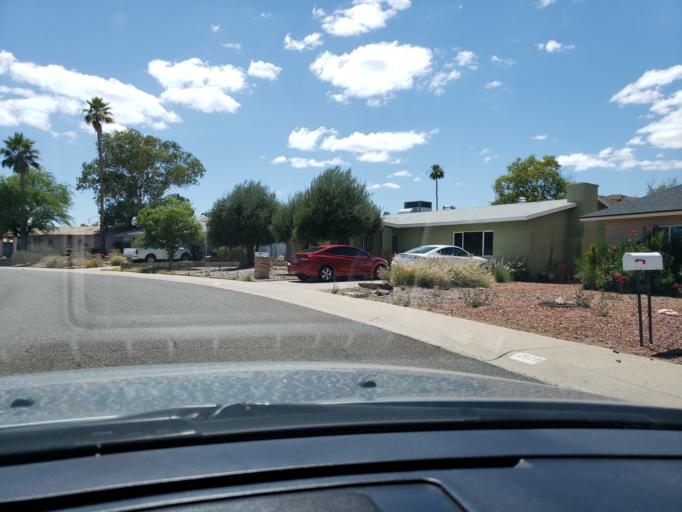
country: US
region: Arizona
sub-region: Maricopa County
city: Paradise Valley
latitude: 33.6055
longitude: -112.0190
